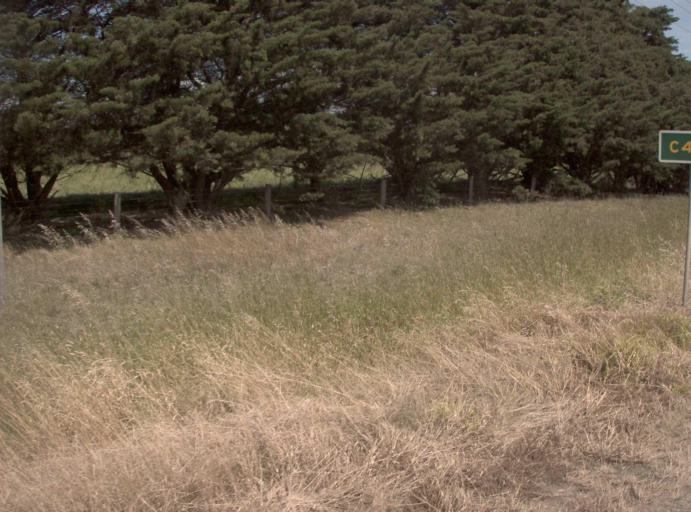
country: AU
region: Victoria
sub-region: Wellington
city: Heyfield
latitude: -37.9923
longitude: 146.8860
